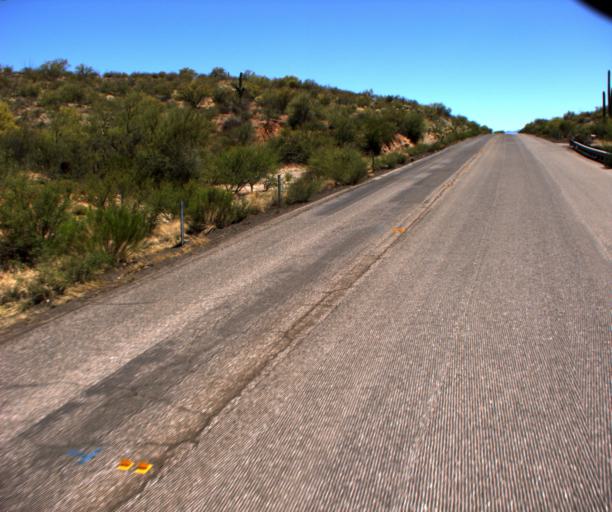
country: US
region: Arizona
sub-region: Pinal County
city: Mammoth
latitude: 32.6861
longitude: -110.6534
